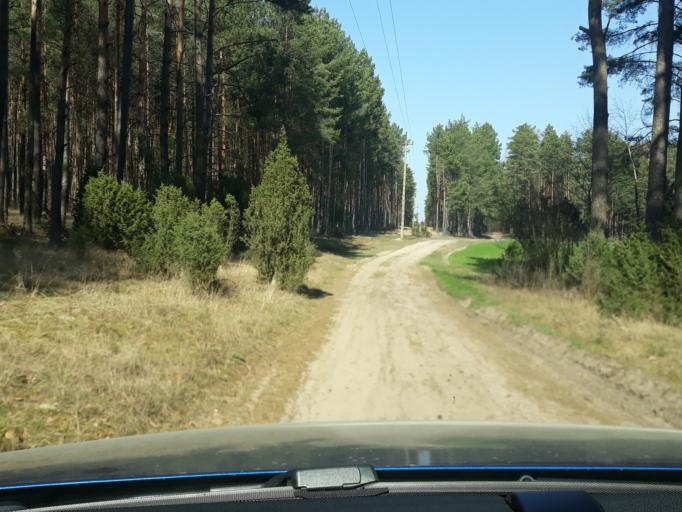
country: PL
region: Pomeranian Voivodeship
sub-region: Powiat bytowski
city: Lipnica
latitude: 53.8667
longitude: 17.4306
